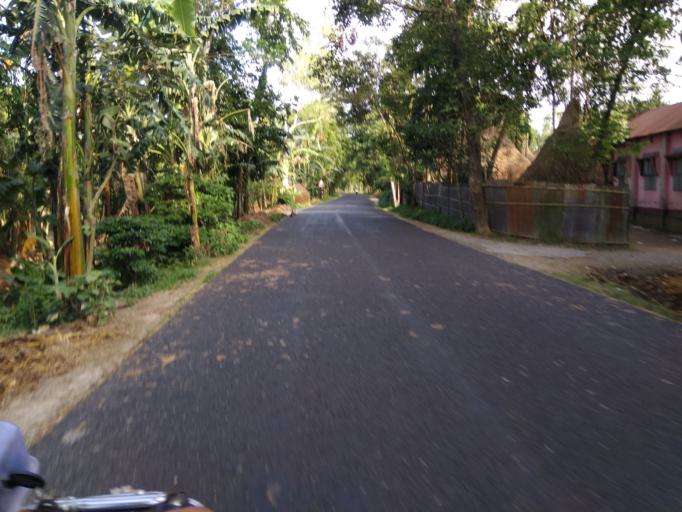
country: BD
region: Rangpur Division
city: Rangpur
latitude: 25.8357
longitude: 89.1153
